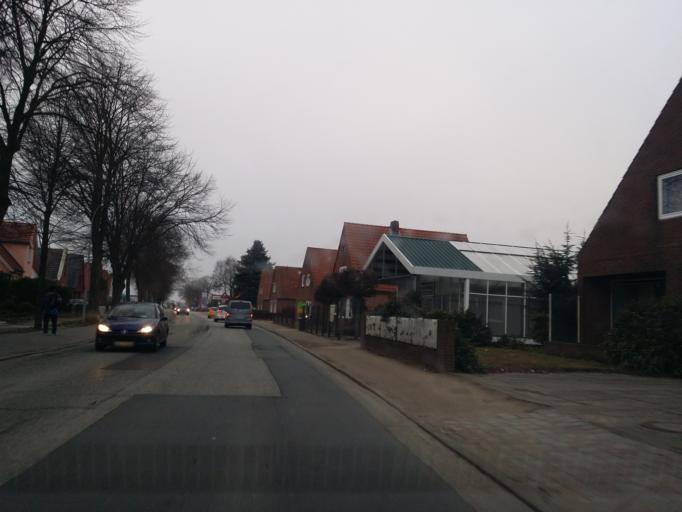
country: DE
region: Schleswig-Holstein
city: Fehmarn
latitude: 54.4421
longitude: 11.1866
